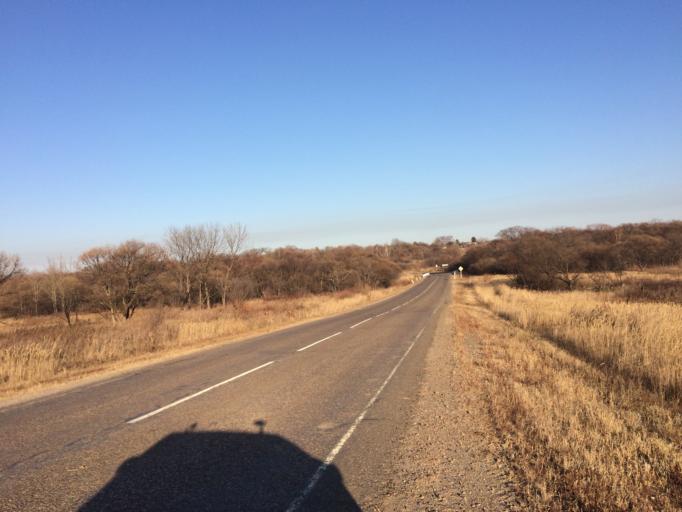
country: RU
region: Primorskiy
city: Ivanovka
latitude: 43.9536
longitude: 132.4602
